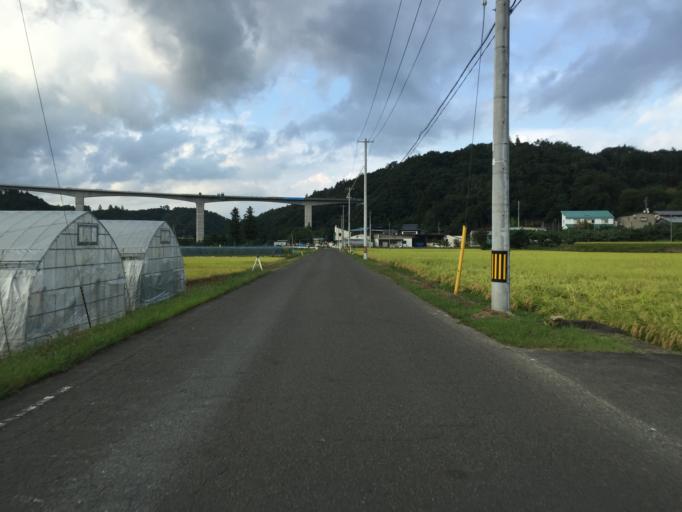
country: JP
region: Fukushima
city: Hobaramachi
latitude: 37.7545
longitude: 140.6108
